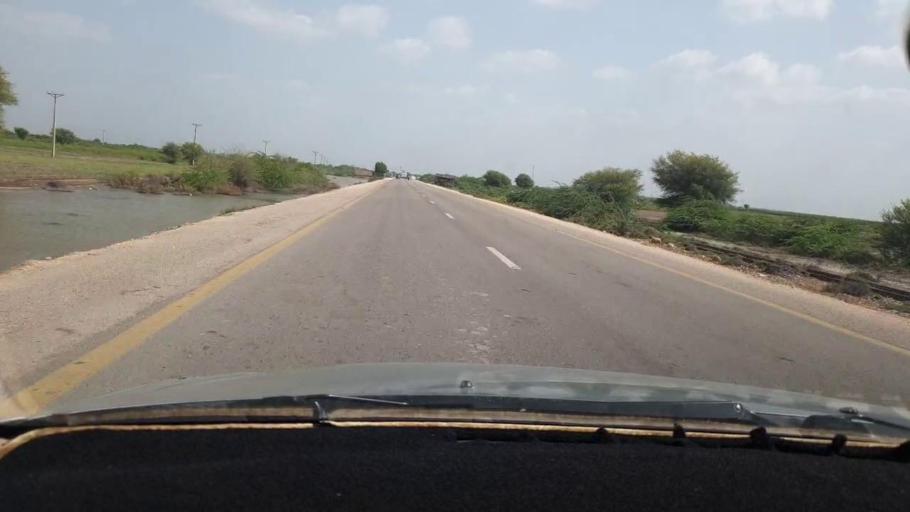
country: PK
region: Sindh
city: Naukot
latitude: 25.0039
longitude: 69.2820
